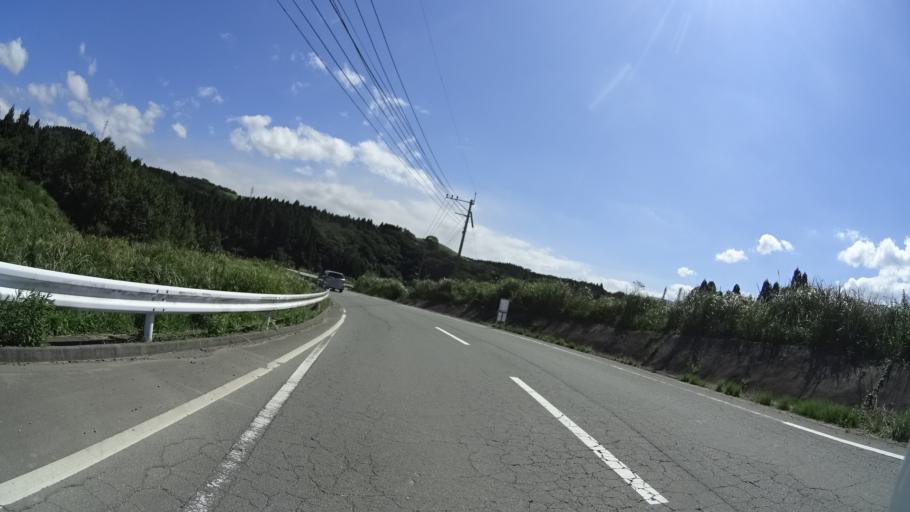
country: JP
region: Kumamoto
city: Aso
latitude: 32.9004
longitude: 130.9947
